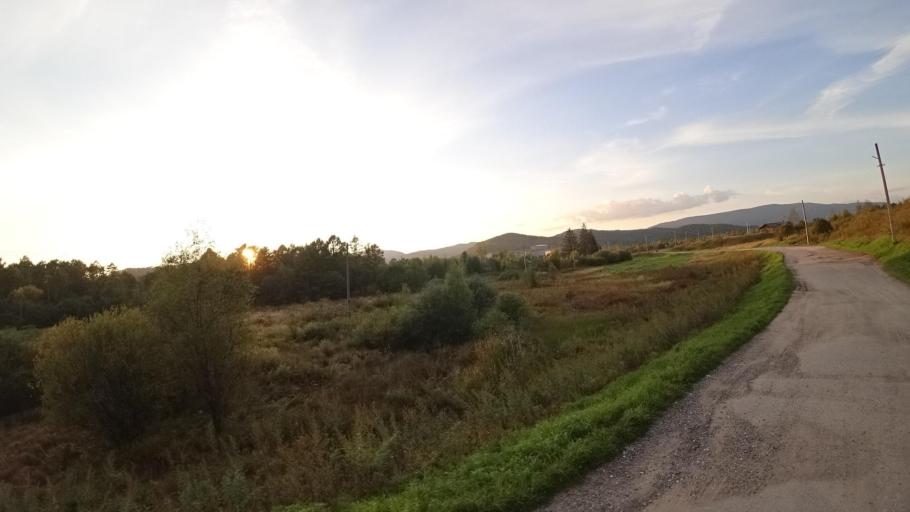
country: RU
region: Jewish Autonomous Oblast
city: Kul'dur
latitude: 49.1970
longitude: 131.6336
